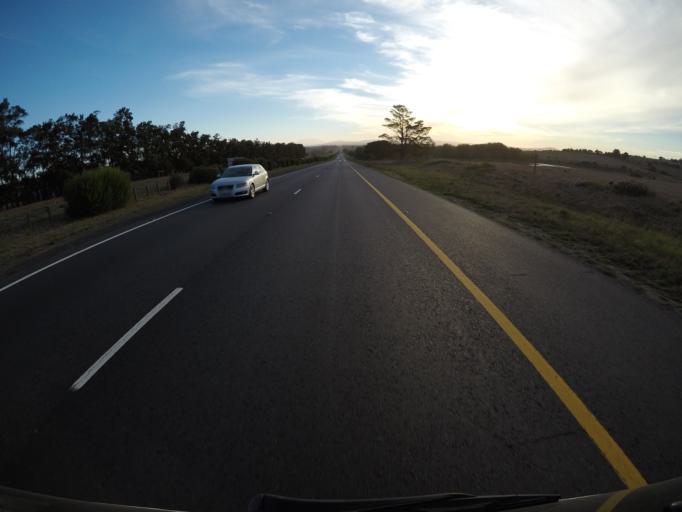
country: ZA
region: Western Cape
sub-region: City of Cape Town
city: Kraaifontein
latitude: -33.8117
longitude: 18.8203
